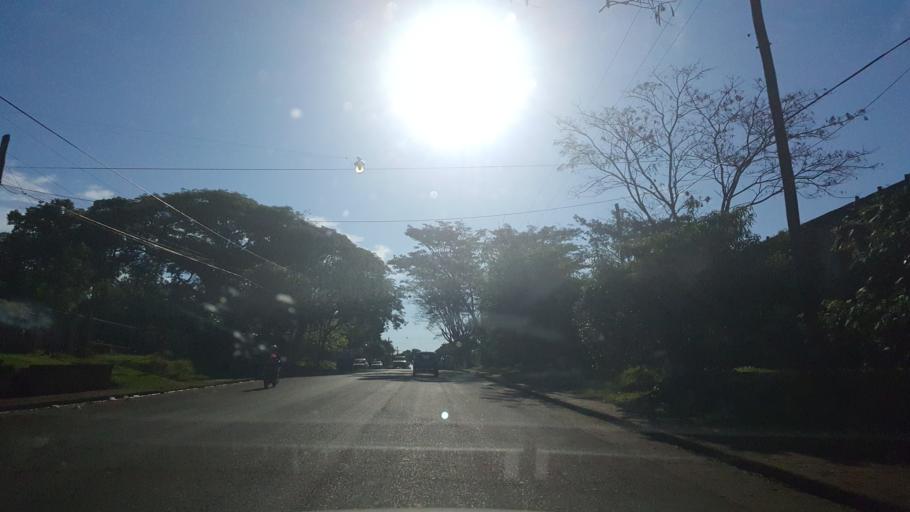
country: AR
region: Misiones
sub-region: Departamento de Capital
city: Posadas
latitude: -27.3830
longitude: -55.9121
